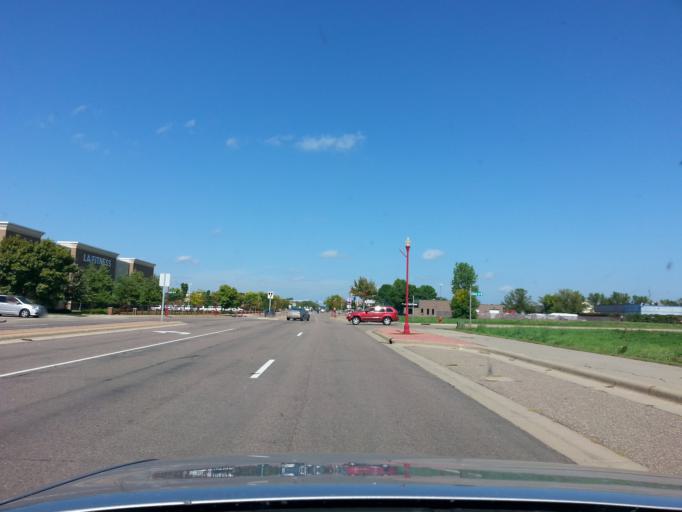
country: US
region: Minnesota
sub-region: Dakota County
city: Apple Valley
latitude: 44.7284
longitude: -93.2074
